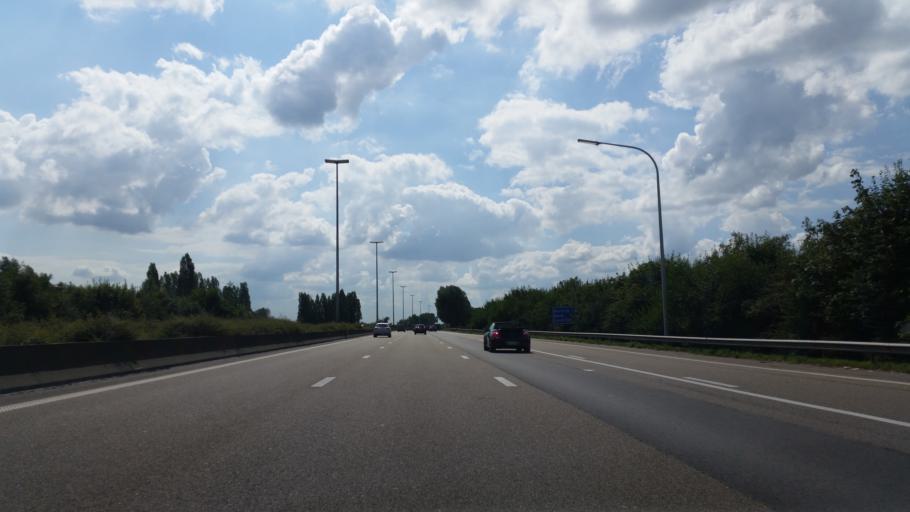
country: BE
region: Flanders
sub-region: Provincie Oost-Vlaanderen
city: Zele
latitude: 51.0857
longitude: 4.0183
